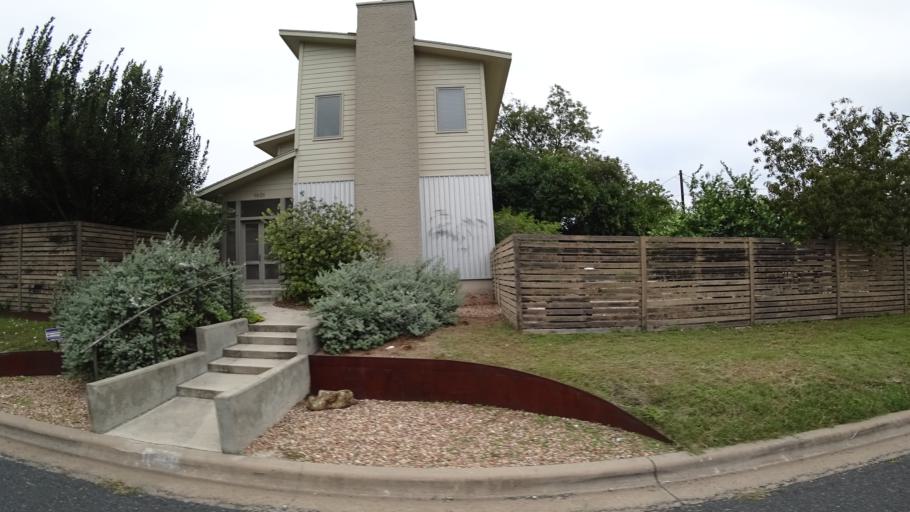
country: US
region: Texas
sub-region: Travis County
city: Austin
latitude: 30.2786
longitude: -97.7230
